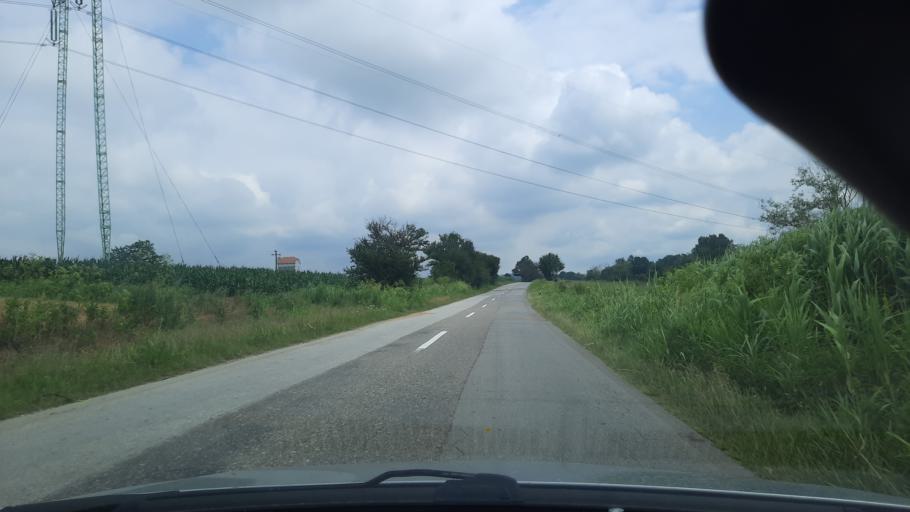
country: RS
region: Central Serbia
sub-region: Branicevski Okrug
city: Malo Crnice
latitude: 44.5787
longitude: 21.3300
